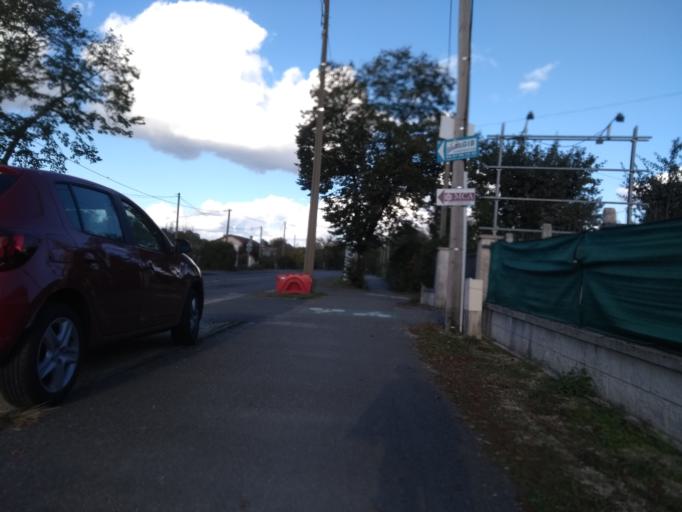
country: FR
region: Aquitaine
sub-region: Departement de la Gironde
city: Cestas
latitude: 44.7383
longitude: -0.6563
